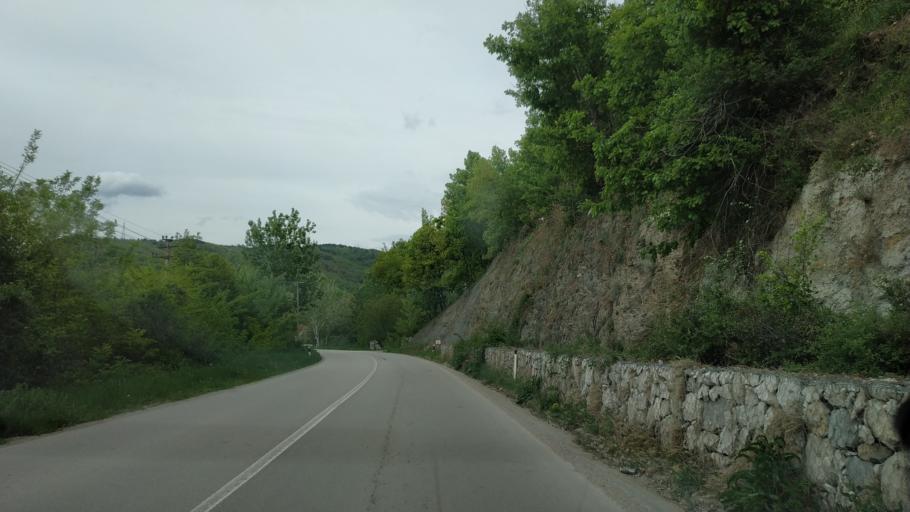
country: RS
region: Central Serbia
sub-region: Nisavski Okrug
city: Aleksinac
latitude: 43.6446
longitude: 21.7131
